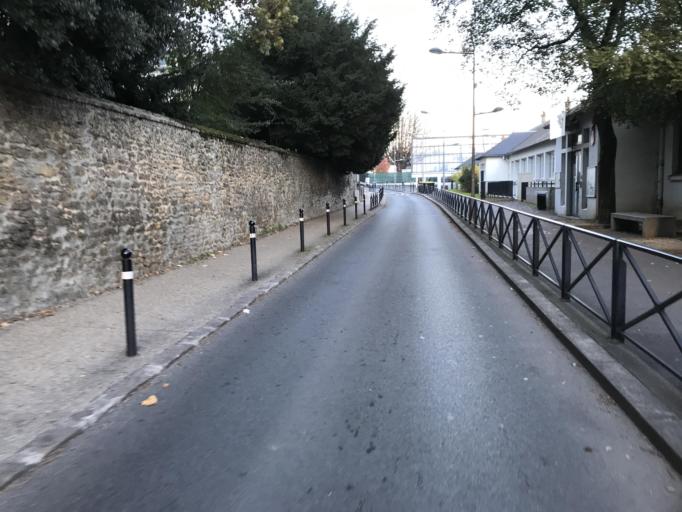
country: FR
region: Ile-de-France
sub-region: Departement de l'Essonne
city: Athis-Mons
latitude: 48.7067
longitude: 2.3865
